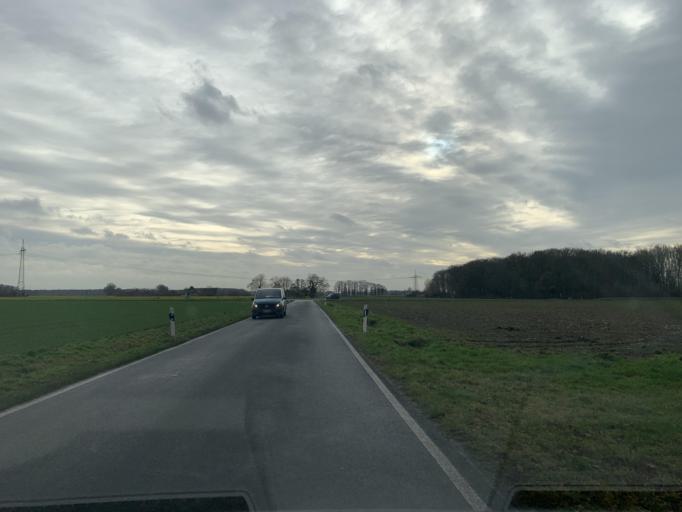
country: DE
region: North Rhine-Westphalia
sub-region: Regierungsbezirk Munster
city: Senden
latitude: 51.8272
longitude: 7.5626
